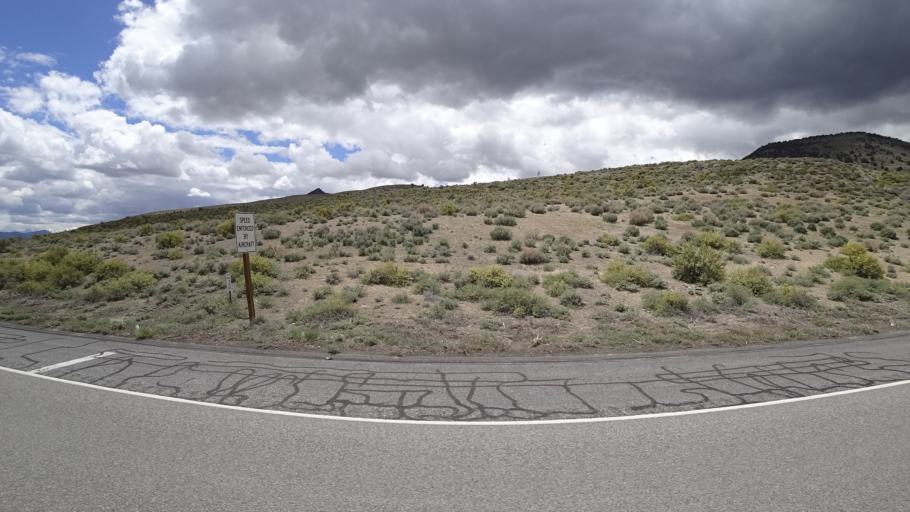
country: US
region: California
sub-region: Mono County
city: Bridgeport
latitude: 37.9494
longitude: -119.1090
